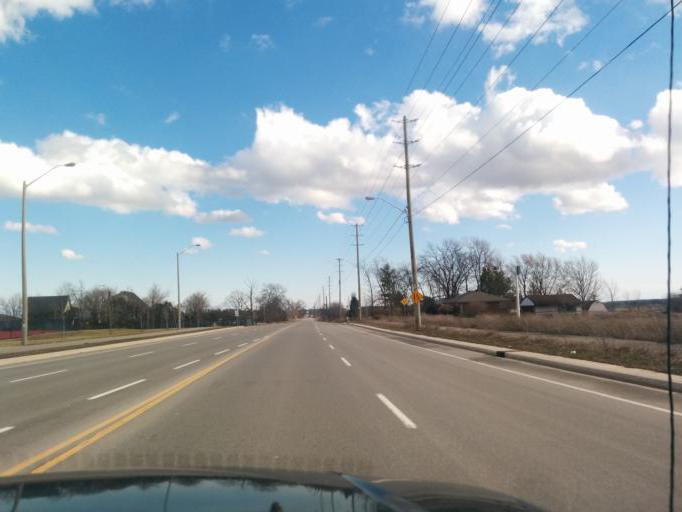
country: CA
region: Ontario
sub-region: Halton
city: Milton
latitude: 43.4857
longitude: -79.8573
